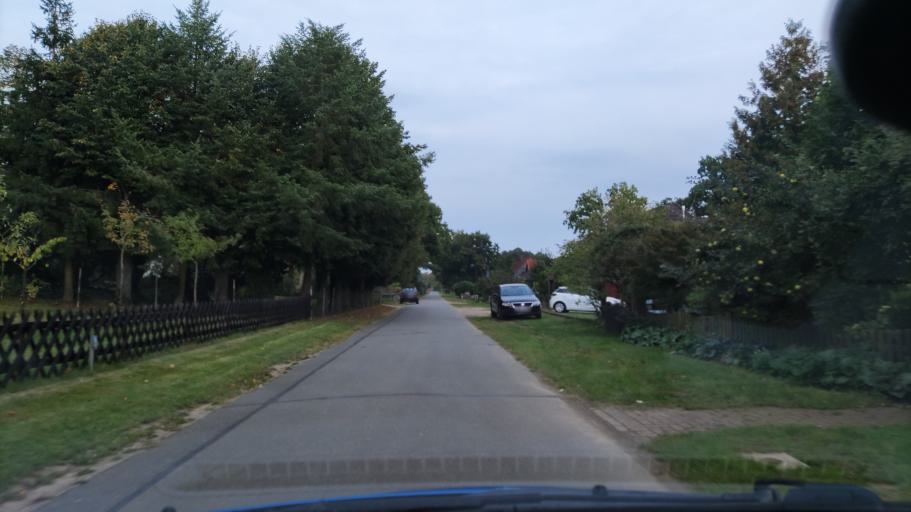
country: DE
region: Lower Saxony
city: Karwitz
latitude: 53.0901
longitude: 10.9952
